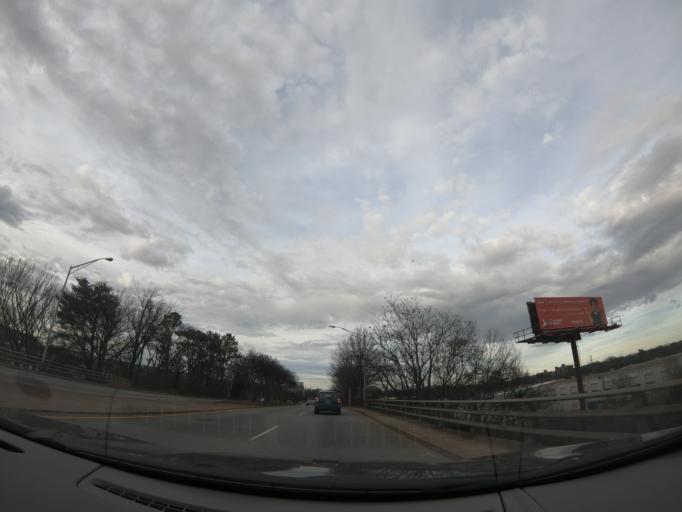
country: US
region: Tennessee
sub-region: Hamilton County
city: Chattanooga
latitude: 35.0235
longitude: -85.3189
